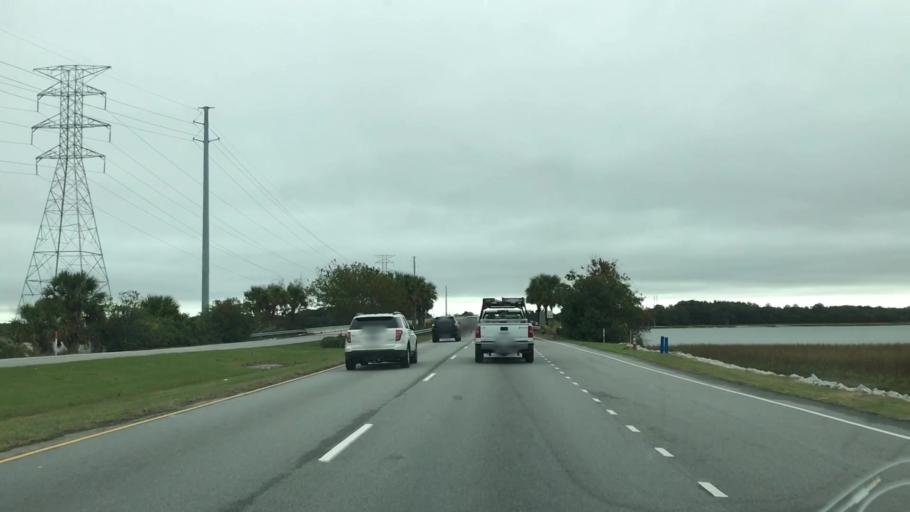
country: US
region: South Carolina
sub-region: Beaufort County
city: Hilton Head Island
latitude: 32.2316
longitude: -80.7950
